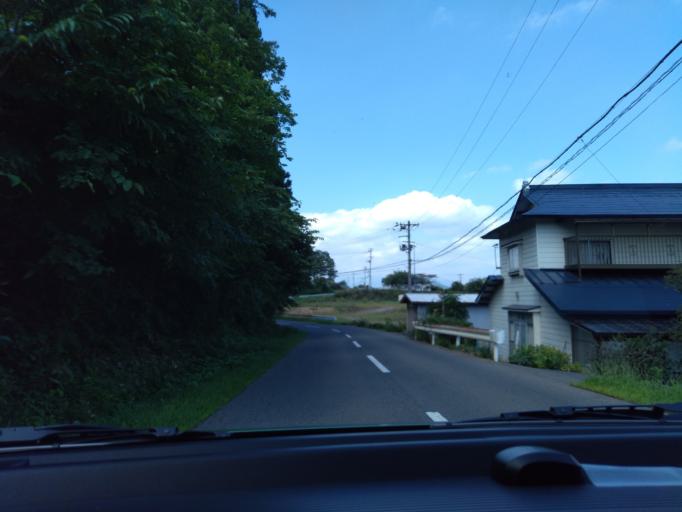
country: JP
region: Iwate
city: Shizukuishi
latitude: 39.6463
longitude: 140.9933
